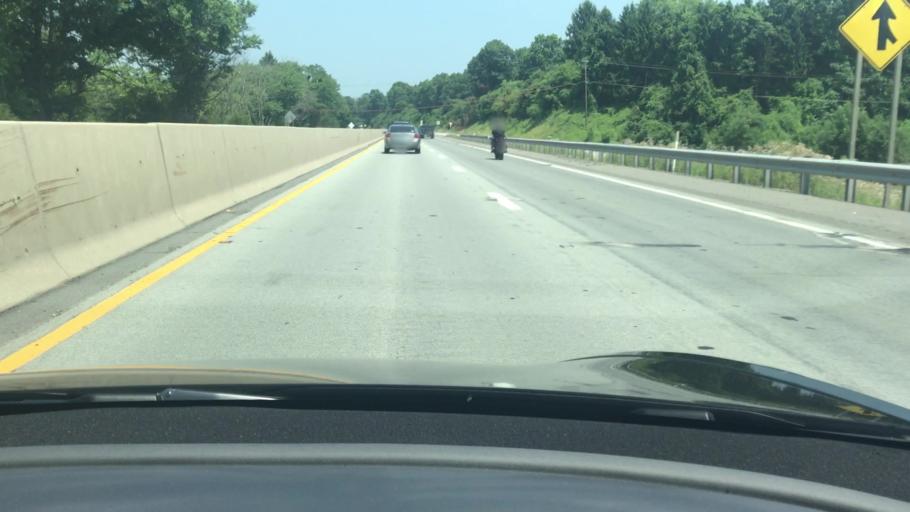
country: US
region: Pennsylvania
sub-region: Perry County
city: Duncannon
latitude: 40.4271
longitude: -77.0105
